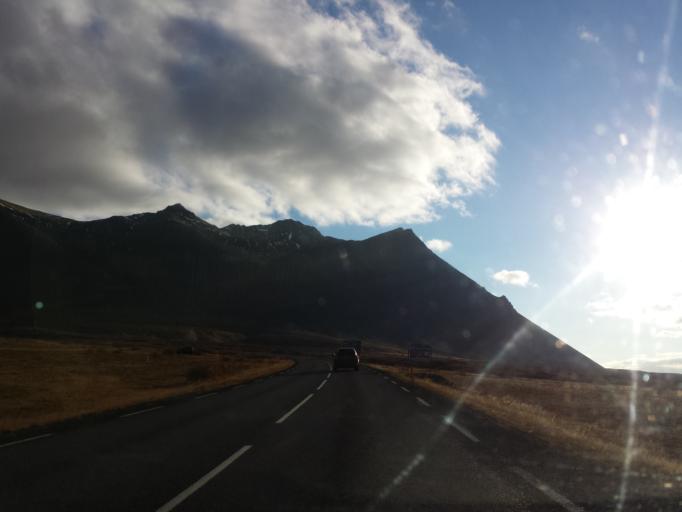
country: IS
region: West
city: Borgarnes
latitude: 64.5234
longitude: -21.8856
